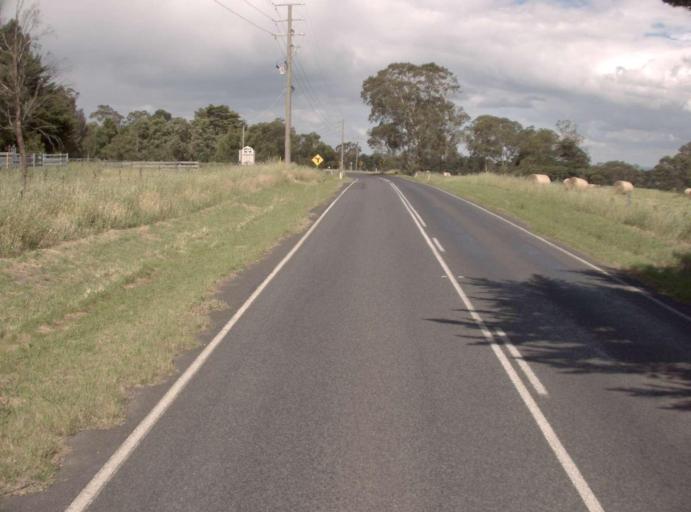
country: AU
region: Victoria
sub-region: Latrobe
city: Traralgon
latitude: -38.1505
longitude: 146.4665
